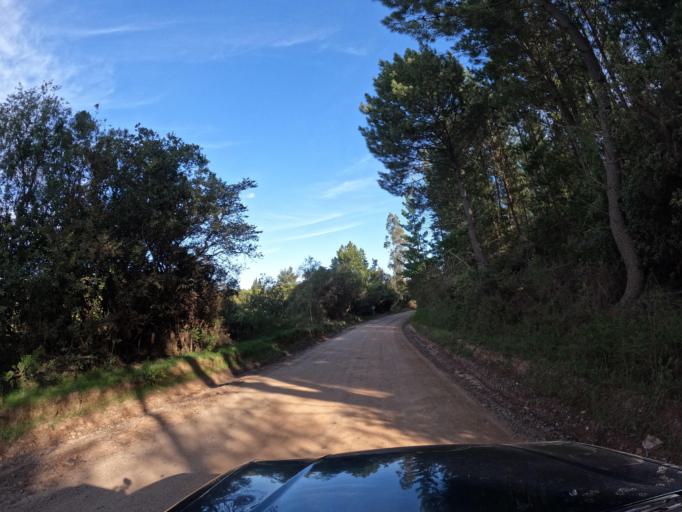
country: CL
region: Biobio
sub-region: Provincia de Biobio
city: La Laja
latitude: -37.1527
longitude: -72.7261
